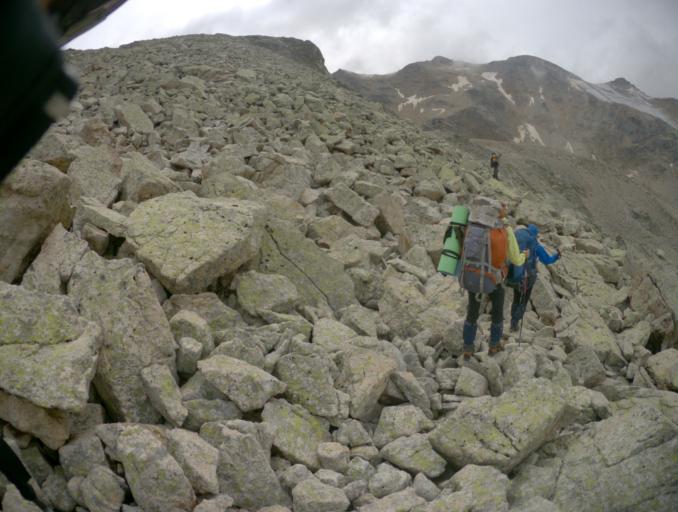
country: RU
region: Karachayevo-Cherkesiya
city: Uchkulan
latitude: 43.2848
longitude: 42.1019
